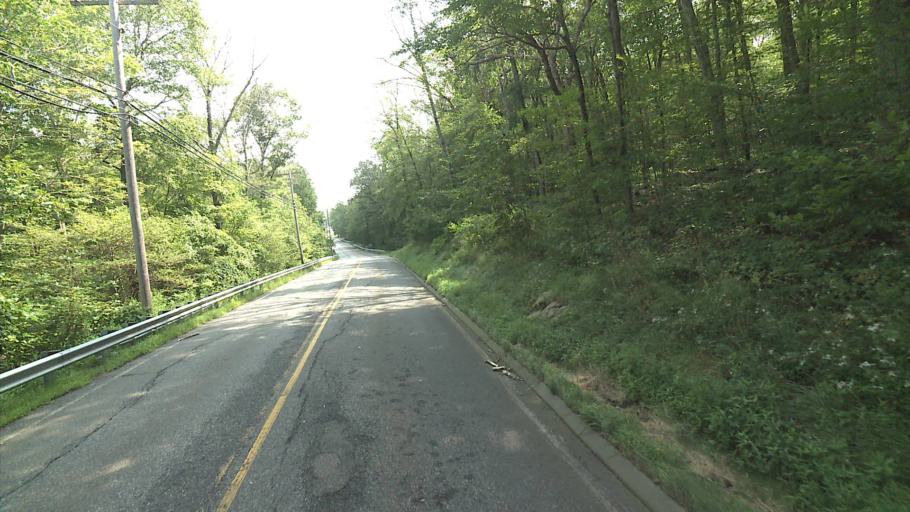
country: US
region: Connecticut
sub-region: New London County
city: Montville Center
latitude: 41.5074
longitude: -72.1552
